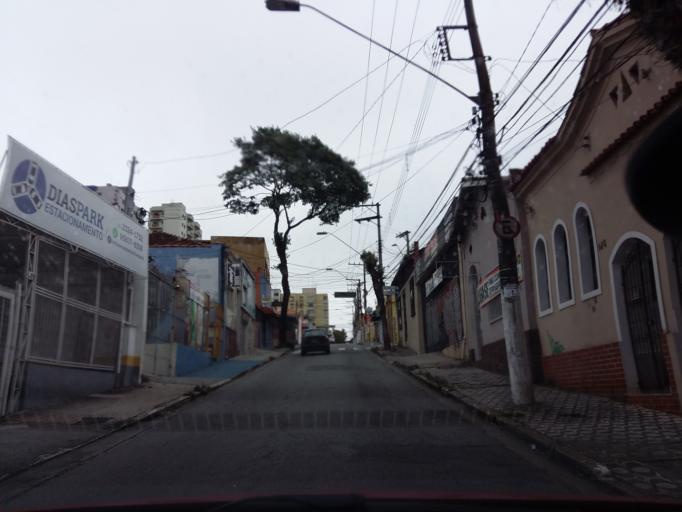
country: BR
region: Sao Paulo
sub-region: Santo Andre
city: Santo Andre
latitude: -23.6667
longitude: -46.5234
